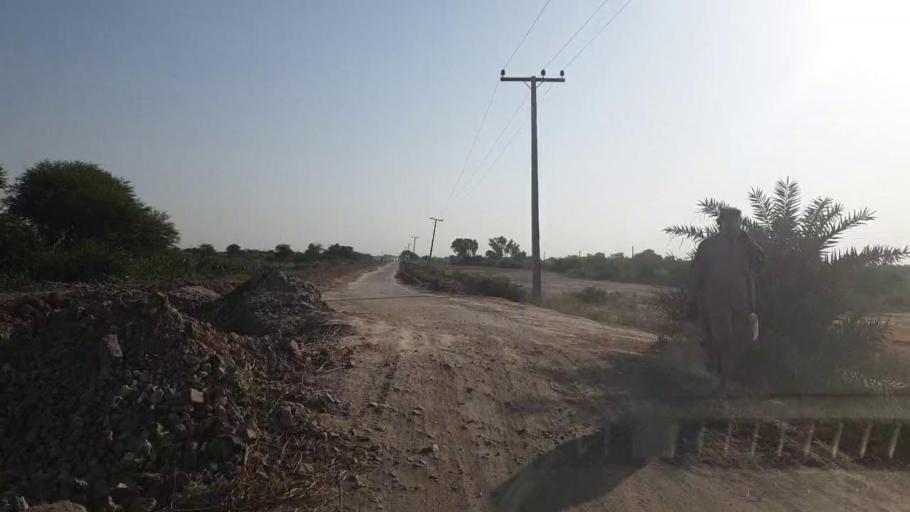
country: PK
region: Sindh
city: Talhar
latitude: 24.9144
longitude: 68.7442
